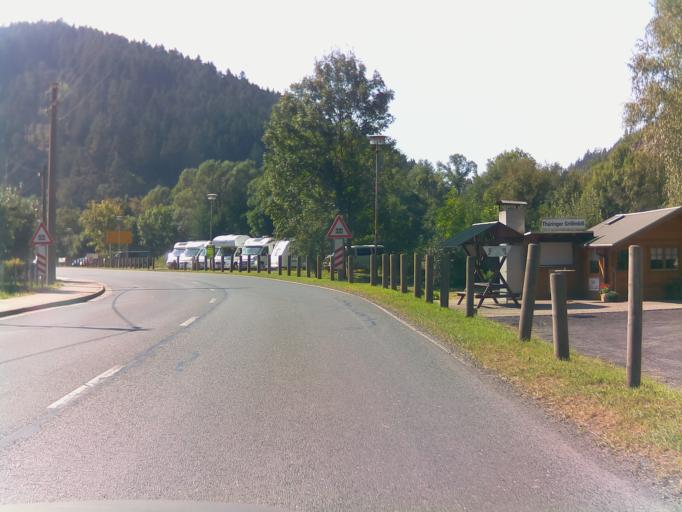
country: DE
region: Thuringia
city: Kaulsdorf
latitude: 50.5969
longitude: 11.4356
